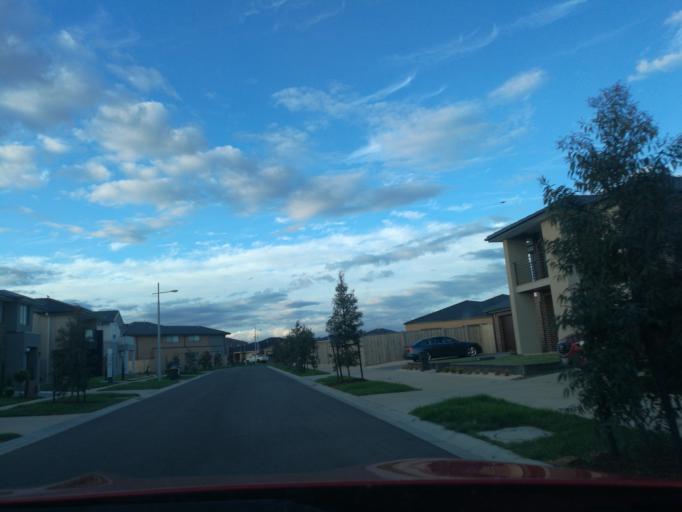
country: AU
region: Victoria
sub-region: Hobsons Bay
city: Altona Meadows
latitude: -37.9169
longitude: 144.7843
